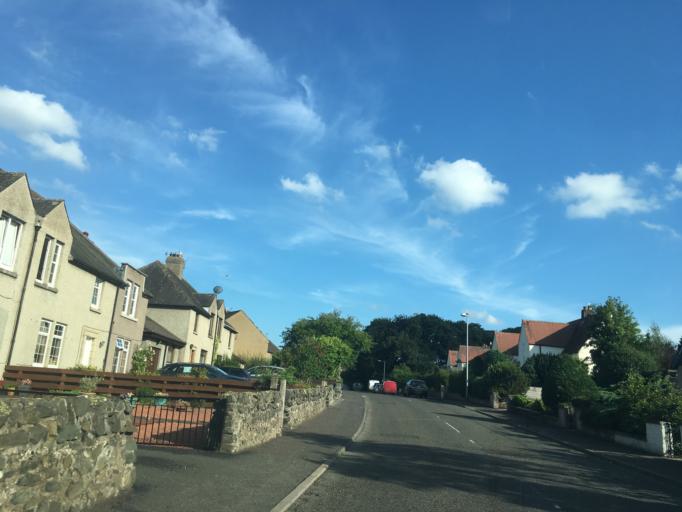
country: GB
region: Scotland
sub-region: The Scottish Borders
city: Peebles
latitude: 55.6455
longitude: -3.1869
